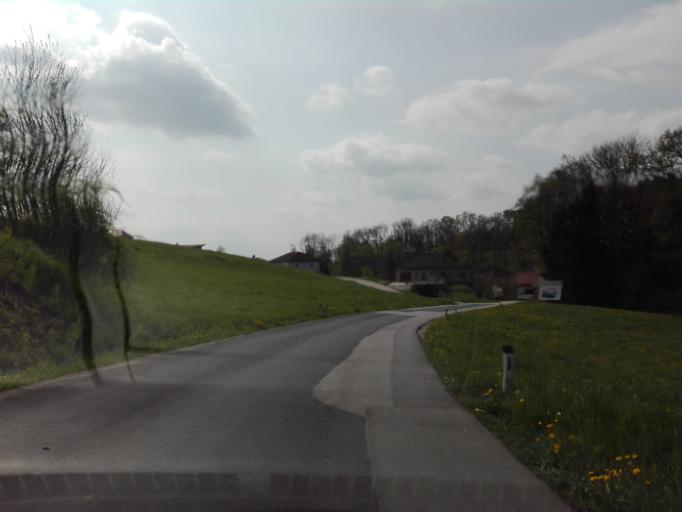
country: AT
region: Upper Austria
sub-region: Politischer Bezirk Perg
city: Perg
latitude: 48.2373
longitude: 14.7041
